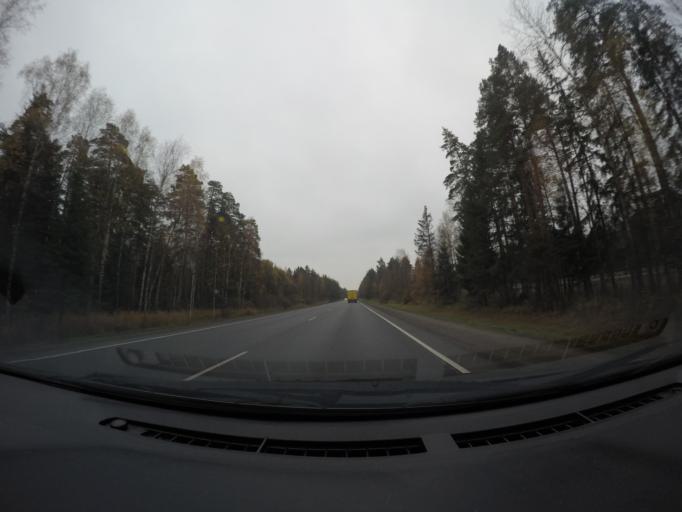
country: RU
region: Moskovskaya
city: Gzhel'
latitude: 55.5550
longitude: 38.3989
